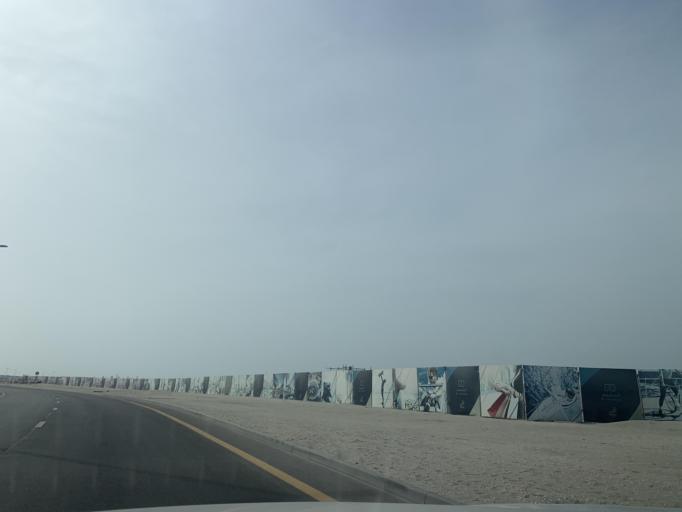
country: BH
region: Muharraq
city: Al Muharraq
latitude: 26.3124
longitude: 50.6409
